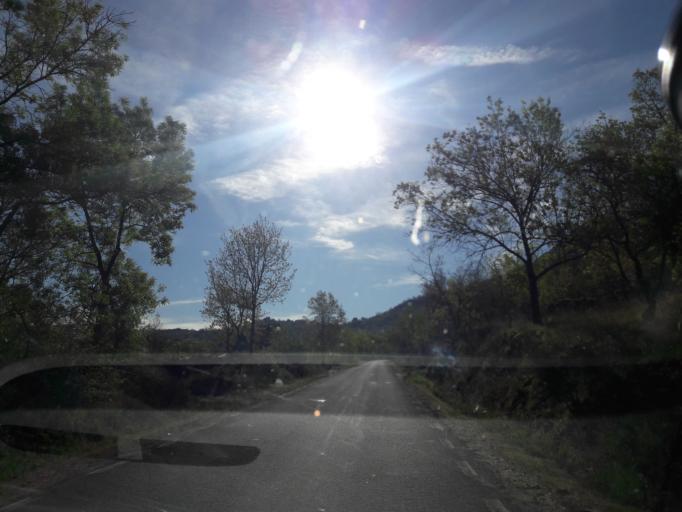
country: ES
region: Castille and Leon
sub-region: Provincia de Salamanca
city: Sanchotello
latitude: 40.4360
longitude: -5.7623
